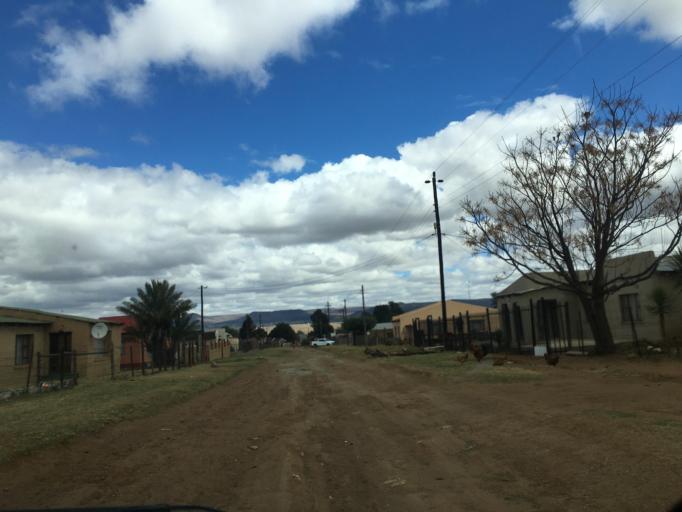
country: ZA
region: Eastern Cape
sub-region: Chris Hani District Municipality
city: Cala
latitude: -31.5310
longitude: 27.6982
